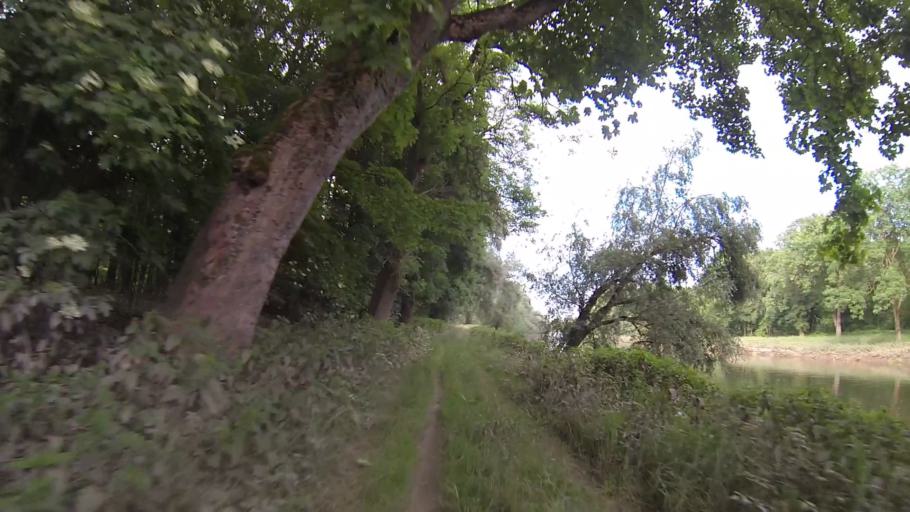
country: DE
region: Baden-Wuerttemberg
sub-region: Tuebingen Region
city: Ulm
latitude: 48.3789
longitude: 9.9660
